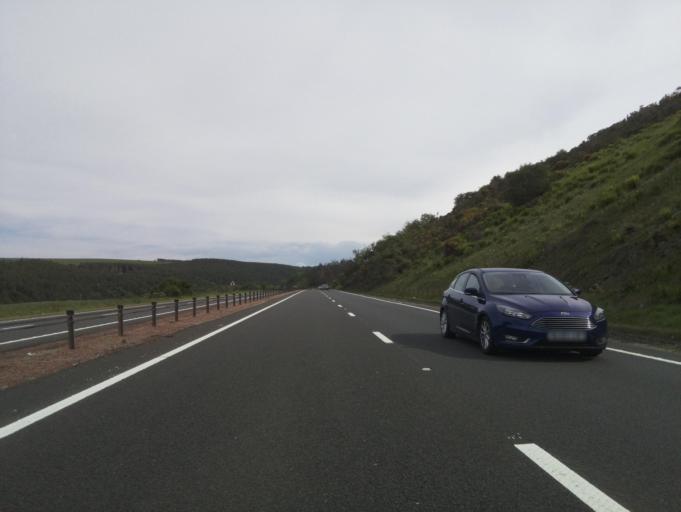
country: GB
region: Scotland
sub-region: The Scottish Borders
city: Duns
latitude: 55.9097
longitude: -2.3364
